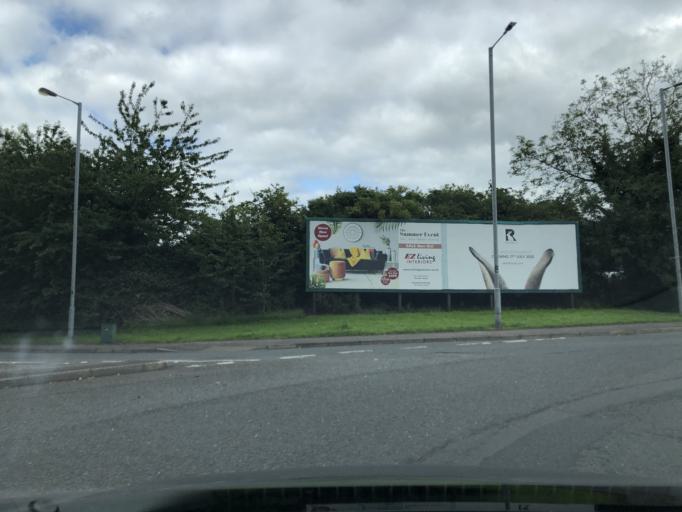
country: GB
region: Northern Ireland
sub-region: Newtownabbey District
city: Newtownabbey
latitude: 54.6548
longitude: -5.9237
